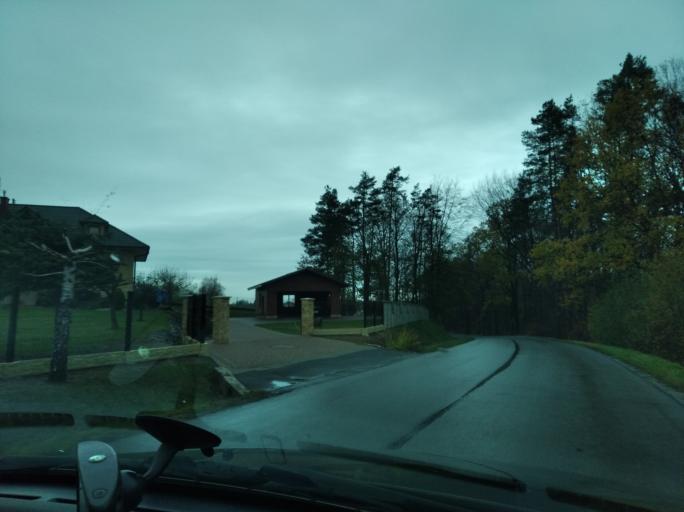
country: PL
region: Subcarpathian Voivodeship
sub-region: Powiat rzeszowski
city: Tyczyn
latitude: 49.9195
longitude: 22.0328
